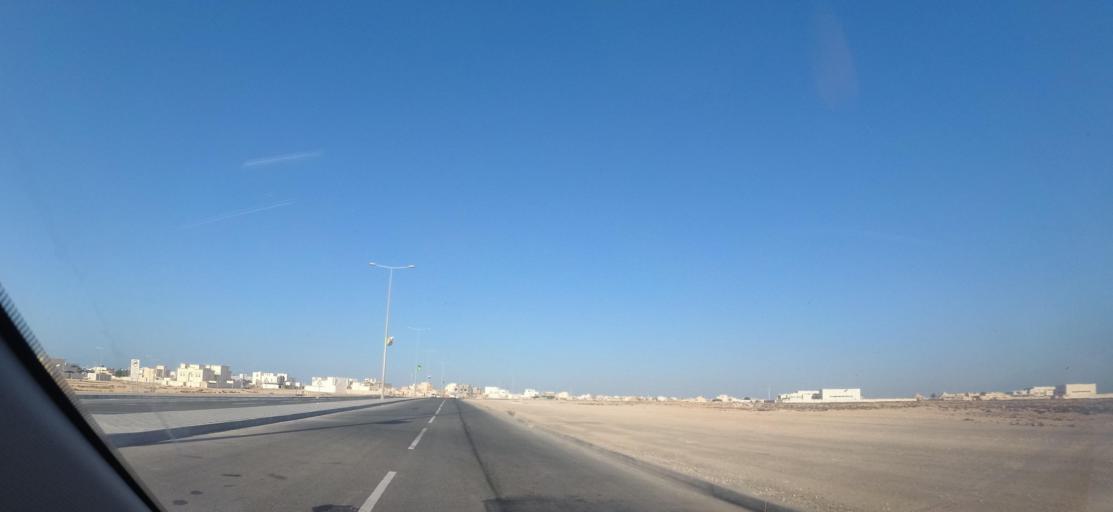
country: QA
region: Madinat ash Shamal
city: Madinat ash Shamal
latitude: 26.1192
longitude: 51.1856
